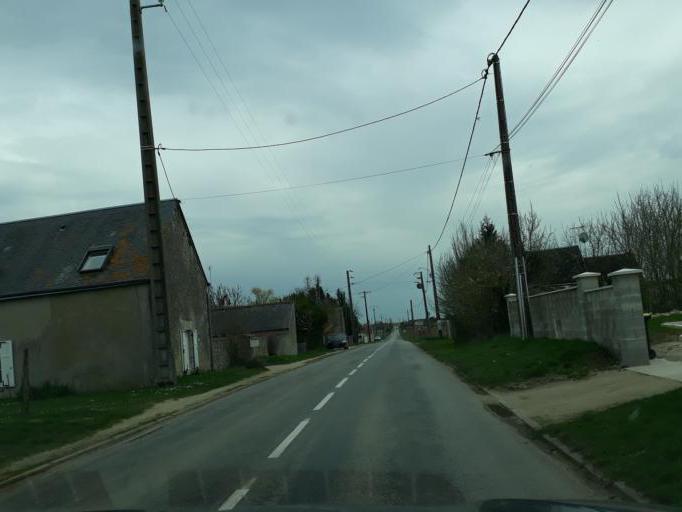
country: FR
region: Centre
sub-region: Departement du Loiret
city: Epieds-en-Beauce
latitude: 47.9166
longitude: 1.6009
